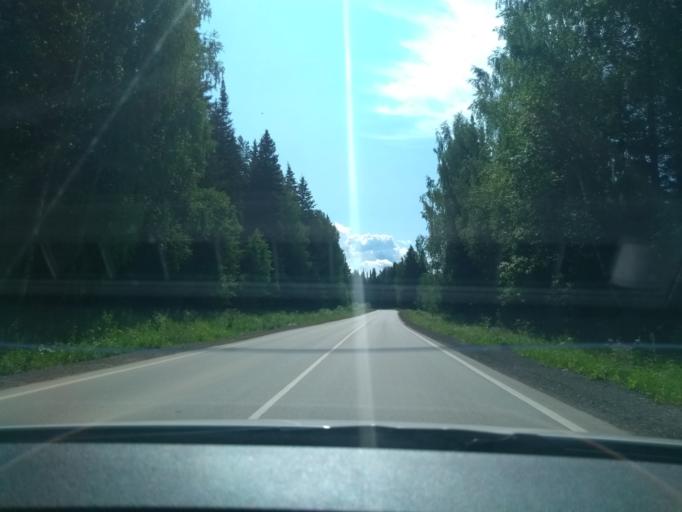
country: RU
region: Perm
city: Bershet'
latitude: 57.8297
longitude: 56.4079
